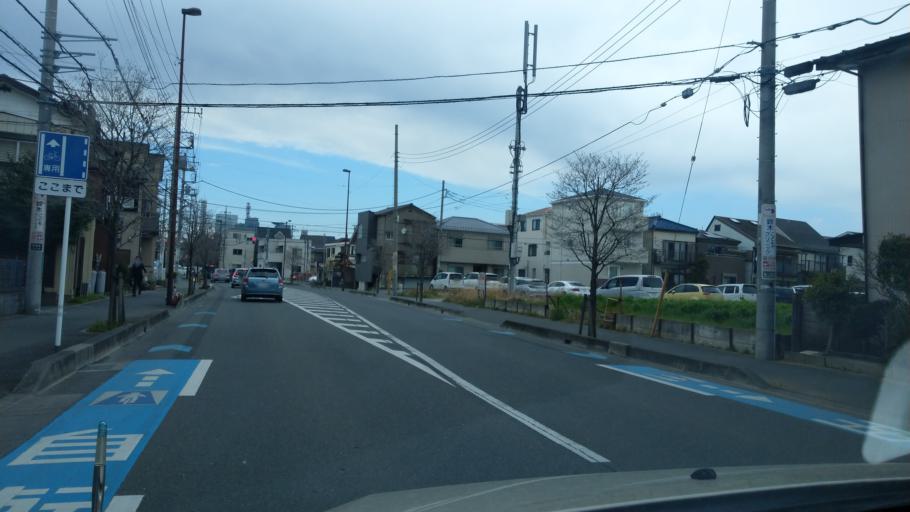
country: JP
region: Saitama
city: Yono
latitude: 35.8732
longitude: 139.6336
